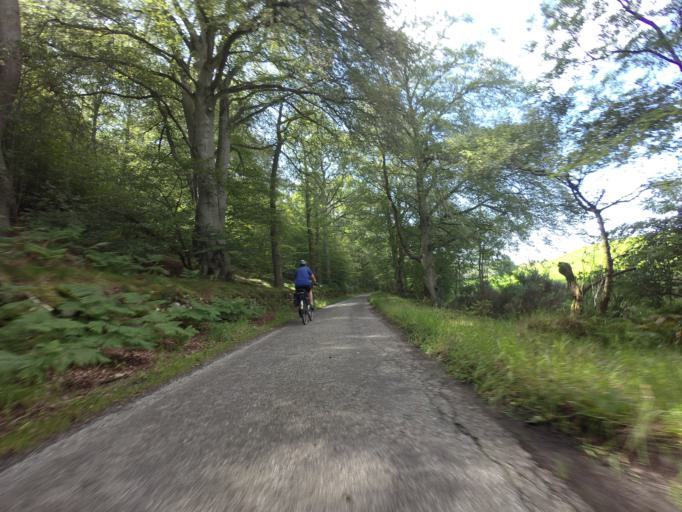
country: GB
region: Scotland
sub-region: Highland
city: Nairn
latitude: 57.5458
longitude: -3.8612
